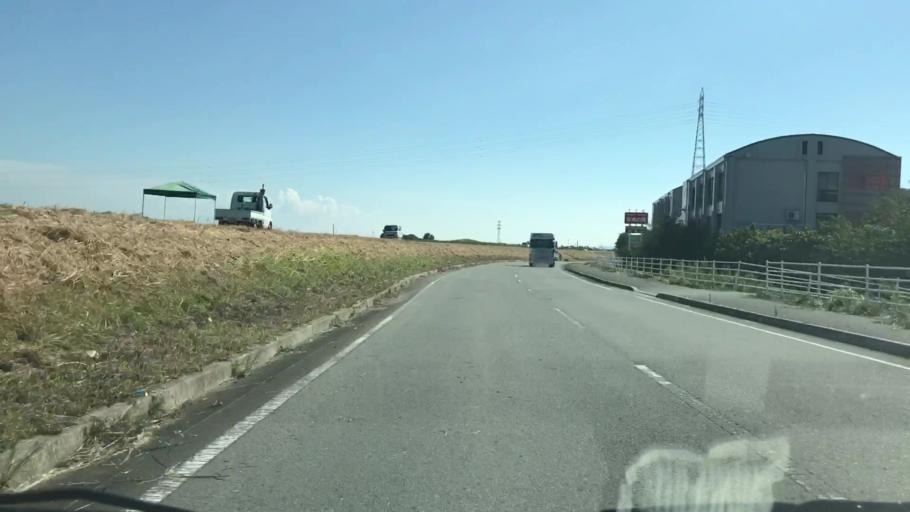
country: JP
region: Saga Prefecture
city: Okawa
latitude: 33.2326
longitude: 130.3783
